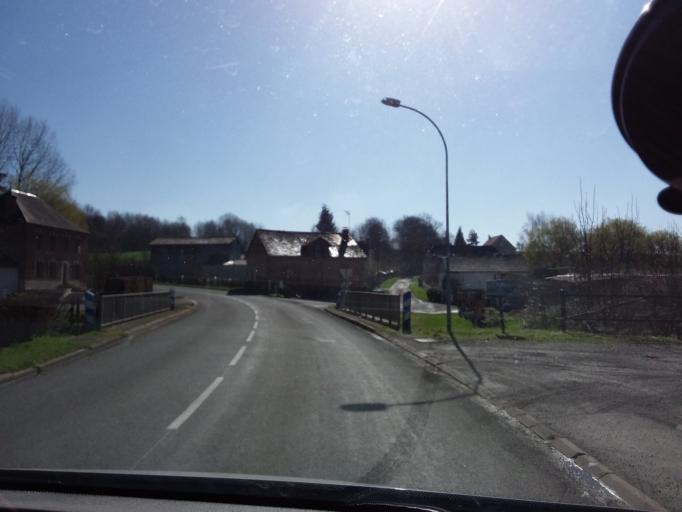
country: FR
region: Picardie
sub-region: Departement de l'Aisne
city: Montcornet
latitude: 49.7380
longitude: 3.9909
